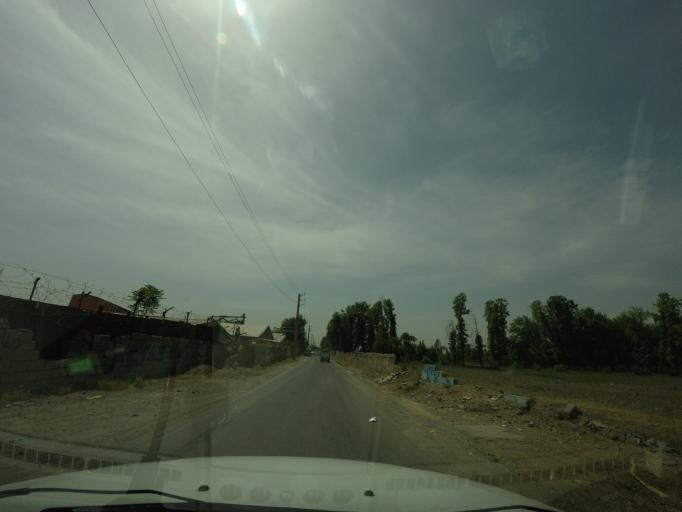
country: IR
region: Tehran
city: Eslamshahr
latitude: 35.6569
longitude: 51.2540
